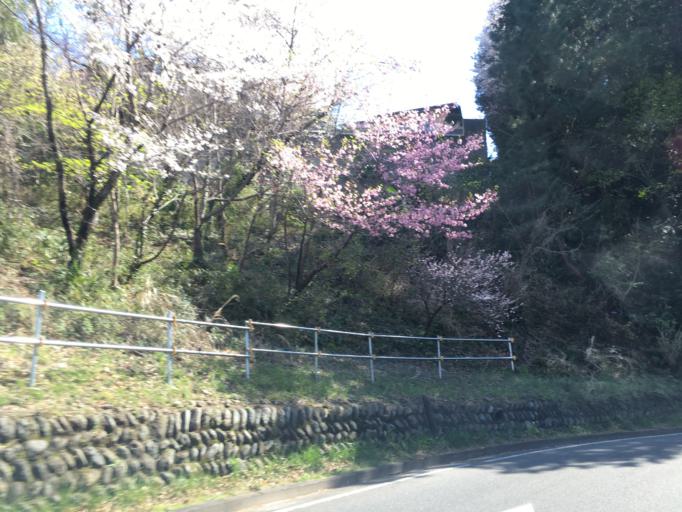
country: JP
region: Tokyo
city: Hino
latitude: 35.6453
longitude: 139.4453
